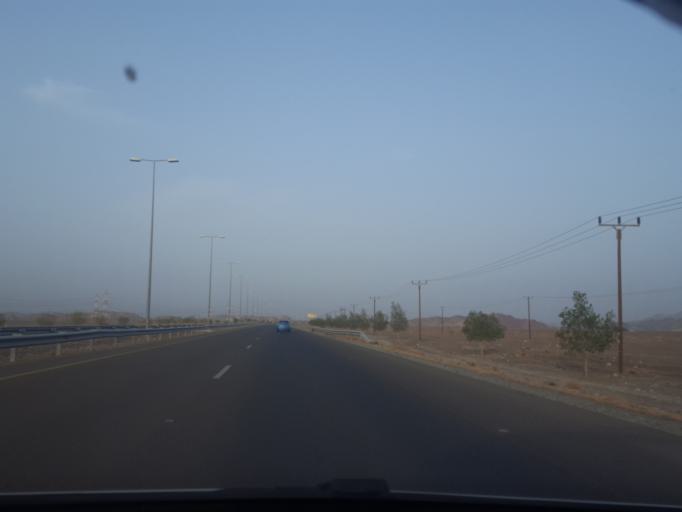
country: OM
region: Al Buraimi
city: Al Buraymi
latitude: 24.2443
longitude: 55.9898
